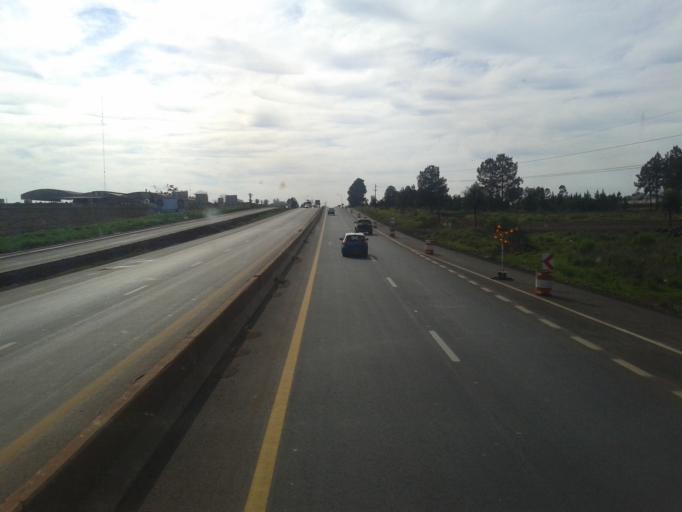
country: AR
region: Misiones
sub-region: Departamento de Candelaria
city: Candelaria
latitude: -27.4689
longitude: -55.7725
